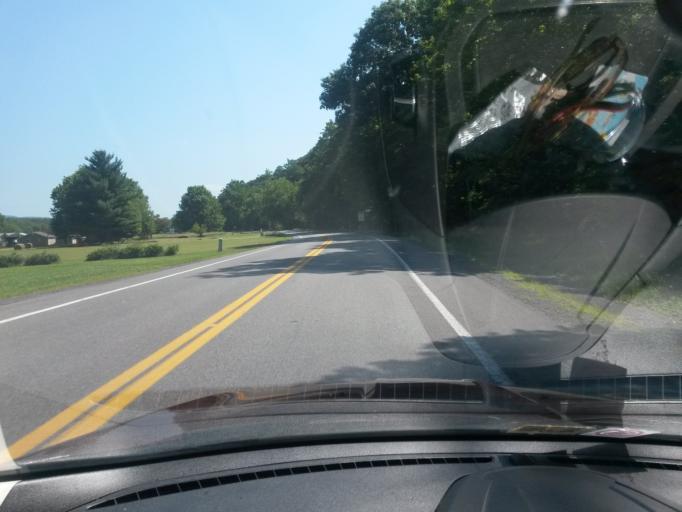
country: US
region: West Virginia
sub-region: Mineral County
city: Keyser
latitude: 39.3614
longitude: -79.0422
